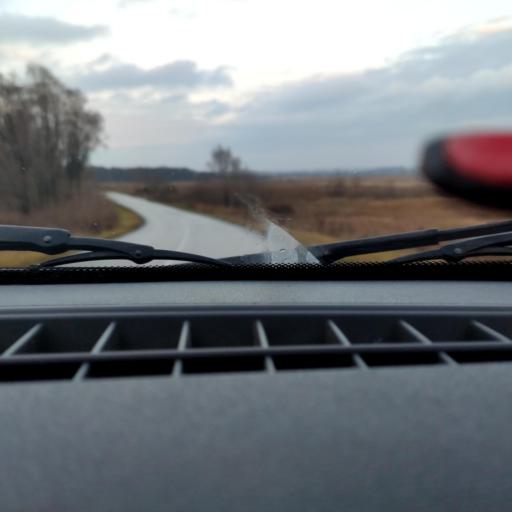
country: RU
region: Bashkortostan
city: Avdon
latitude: 54.5099
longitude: 55.8563
